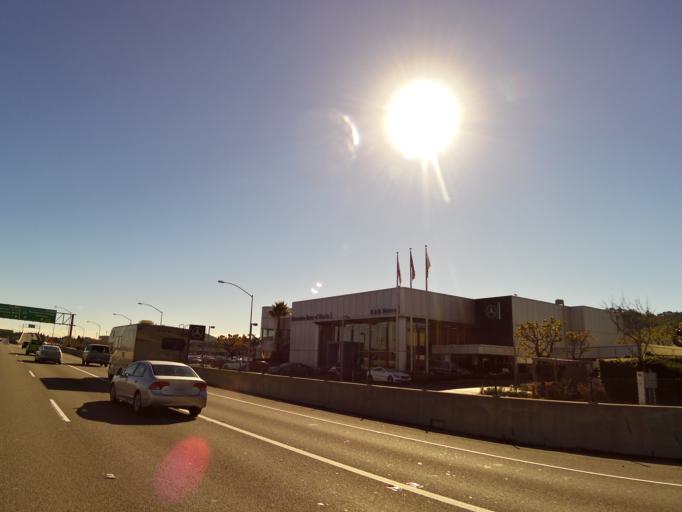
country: US
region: California
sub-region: Marin County
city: San Rafael
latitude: 37.9658
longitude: -122.5160
